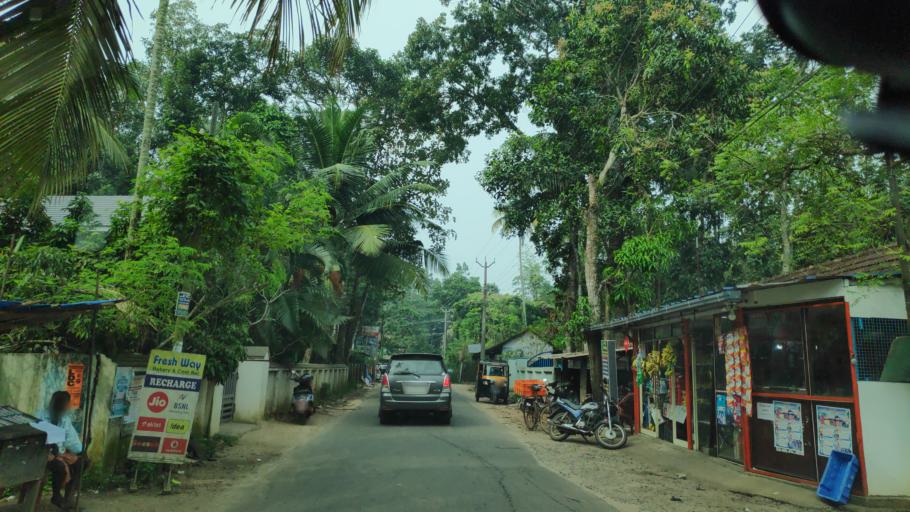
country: IN
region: Kerala
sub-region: Alappuzha
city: Alleppey
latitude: 9.5711
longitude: 76.3356
